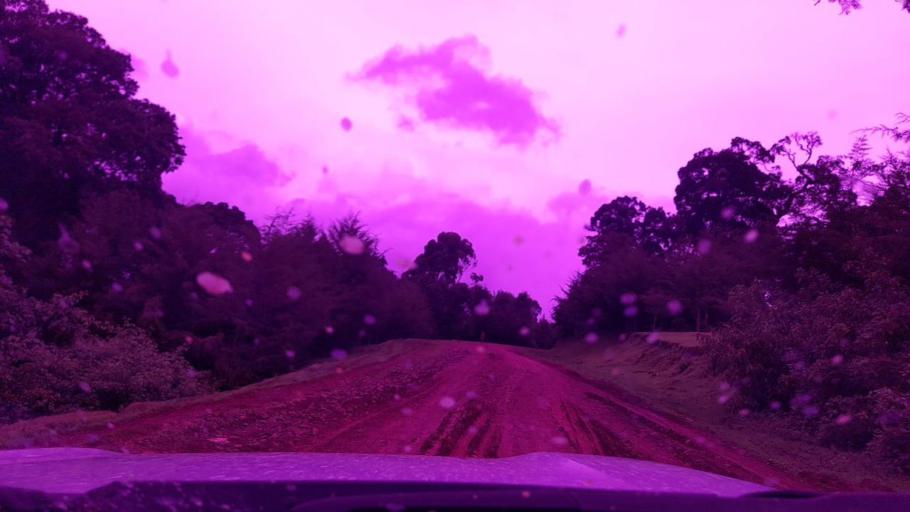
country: ET
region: Southern Nations, Nationalities, and People's Region
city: Tippi
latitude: 7.5726
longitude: 35.6636
